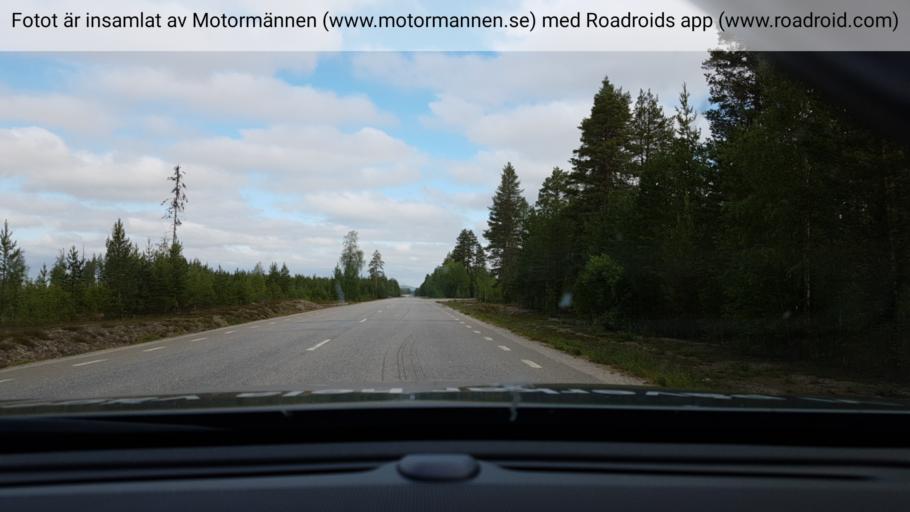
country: SE
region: Vaesterbotten
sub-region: Norsjo Kommun
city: Norsjoe
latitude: 64.5580
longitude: 19.3216
